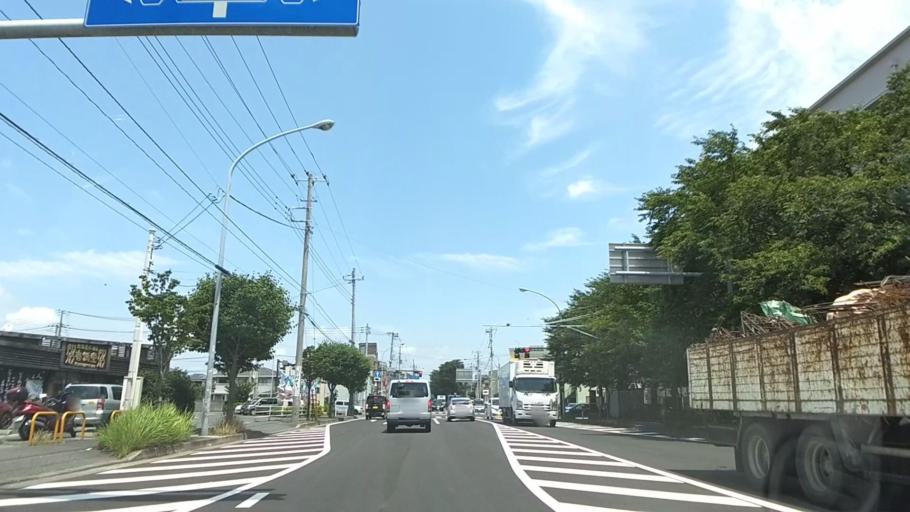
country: JP
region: Kanagawa
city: Minami-rinkan
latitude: 35.4718
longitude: 139.4807
